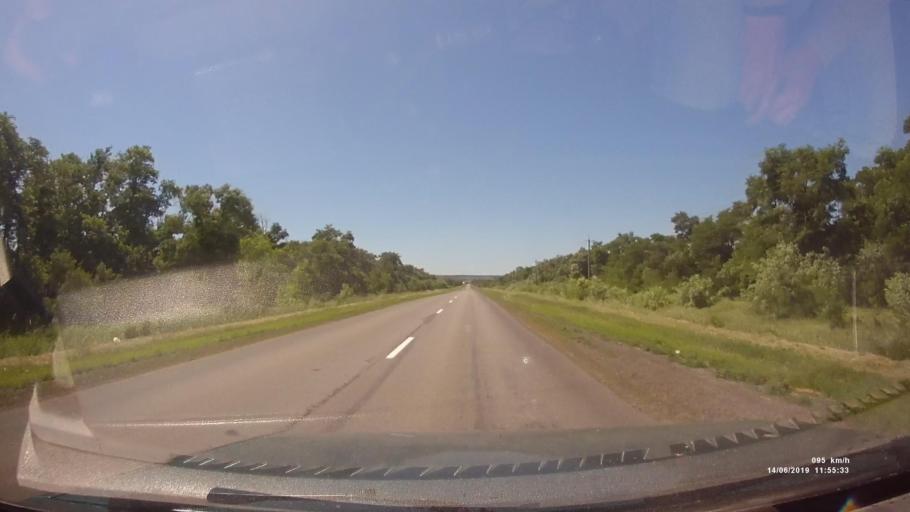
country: RU
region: Rostov
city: Kazanskaya
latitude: 49.8096
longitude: 41.1751
